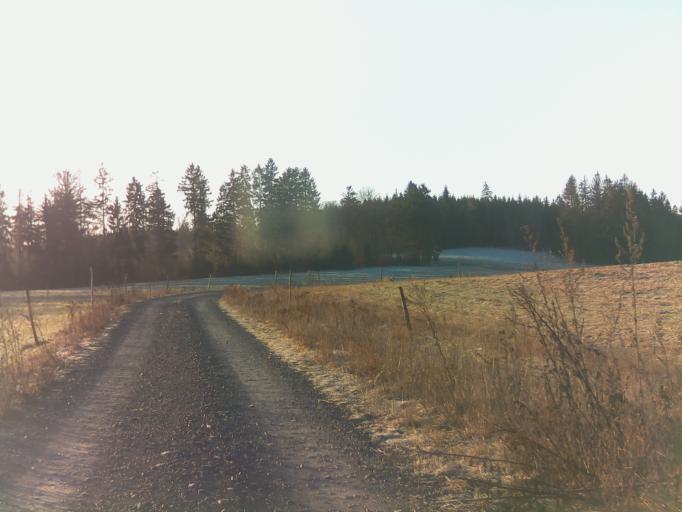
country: DE
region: Thuringia
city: Judenbach
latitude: 50.3836
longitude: 11.2122
